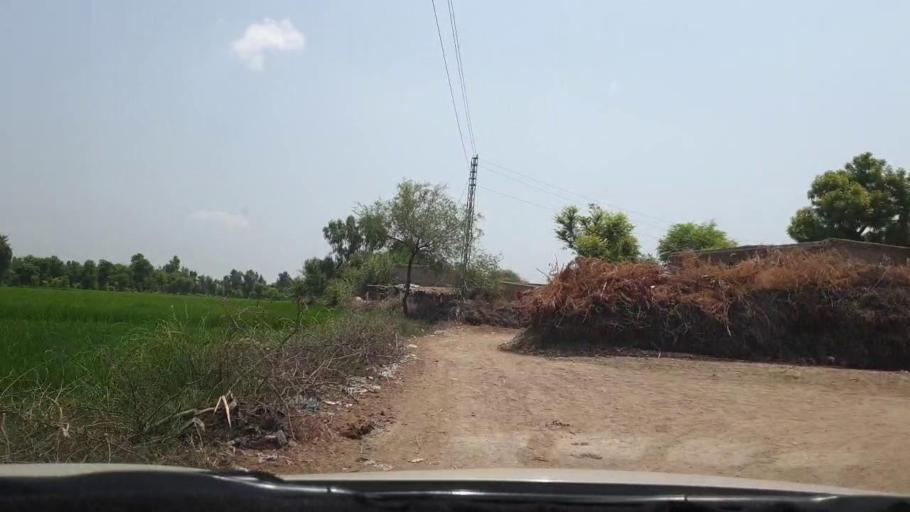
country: PK
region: Sindh
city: New Badah
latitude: 27.2966
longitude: 68.0722
